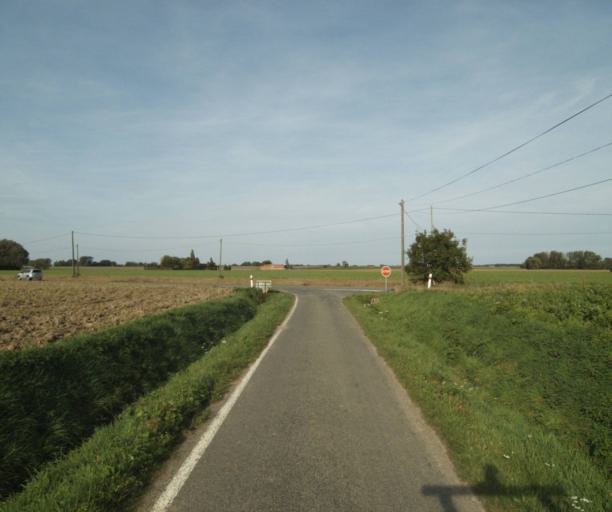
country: FR
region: Nord-Pas-de-Calais
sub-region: Departement du Nord
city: Fournes-en-Weppes
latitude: 50.5962
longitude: 2.8733
